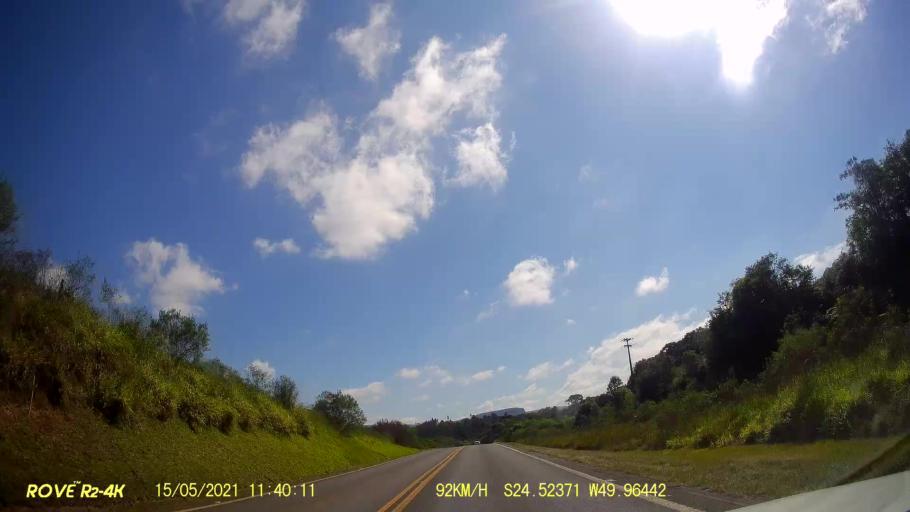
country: BR
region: Parana
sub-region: Pirai Do Sul
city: Pirai do Sul
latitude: -24.5237
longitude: -49.9644
